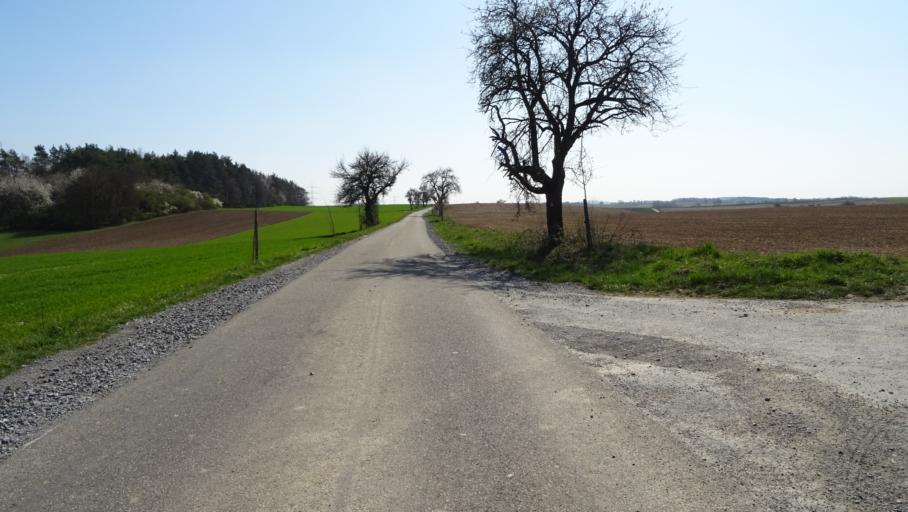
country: DE
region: Baden-Wuerttemberg
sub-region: Karlsruhe Region
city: Billigheim
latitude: 49.4007
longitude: 9.2462
